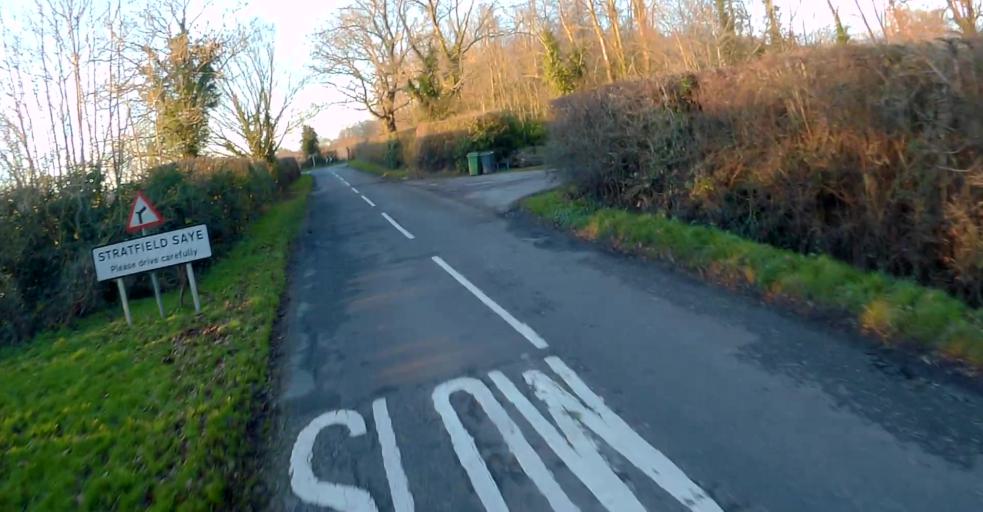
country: GB
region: England
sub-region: West Berkshire
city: Stratfield Mortimer
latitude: 51.3465
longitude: -1.0088
